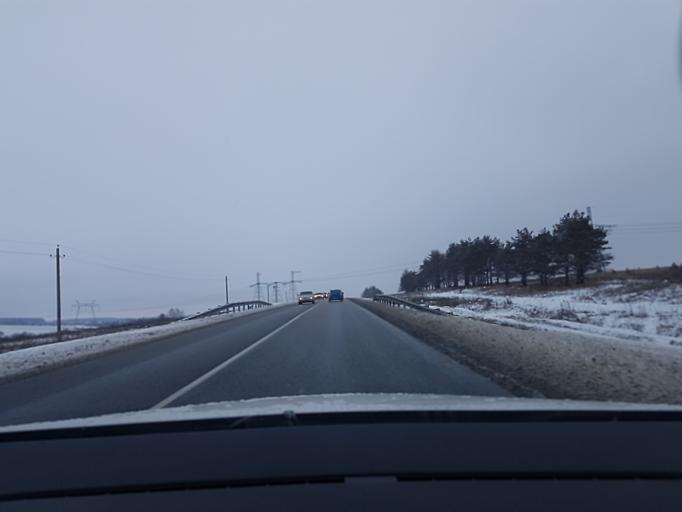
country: RU
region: Moskovskaya
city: Ozherel'ye
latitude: 54.7233
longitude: 38.2740
